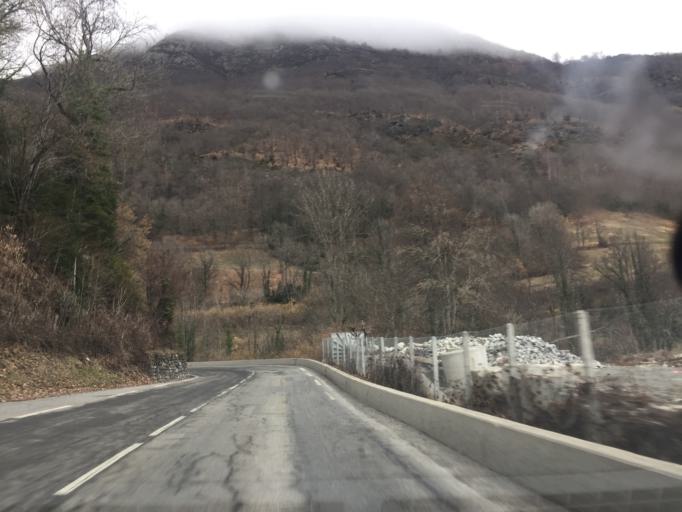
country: FR
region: Midi-Pyrenees
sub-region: Departement des Hautes-Pyrenees
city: Saint-Lary-Soulan
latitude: 42.7986
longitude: 0.2916
